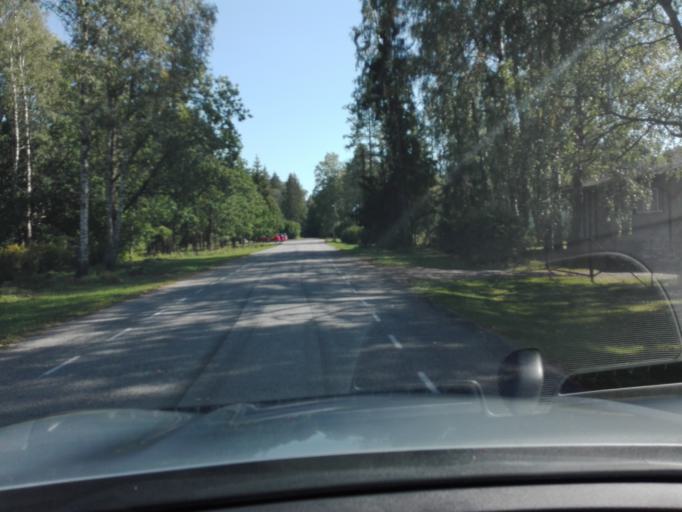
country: EE
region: Raplamaa
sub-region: Rapla vald
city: Rapla
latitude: 59.0656
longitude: 24.8069
